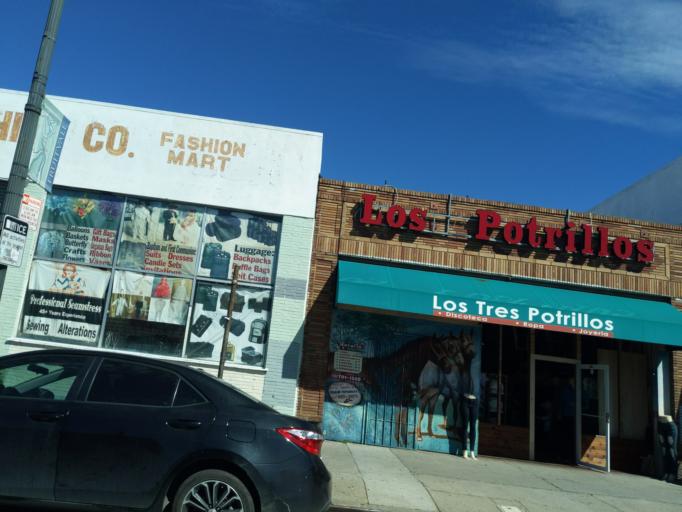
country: US
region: California
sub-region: Alameda County
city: Alameda
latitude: 37.7741
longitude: -122.2182
